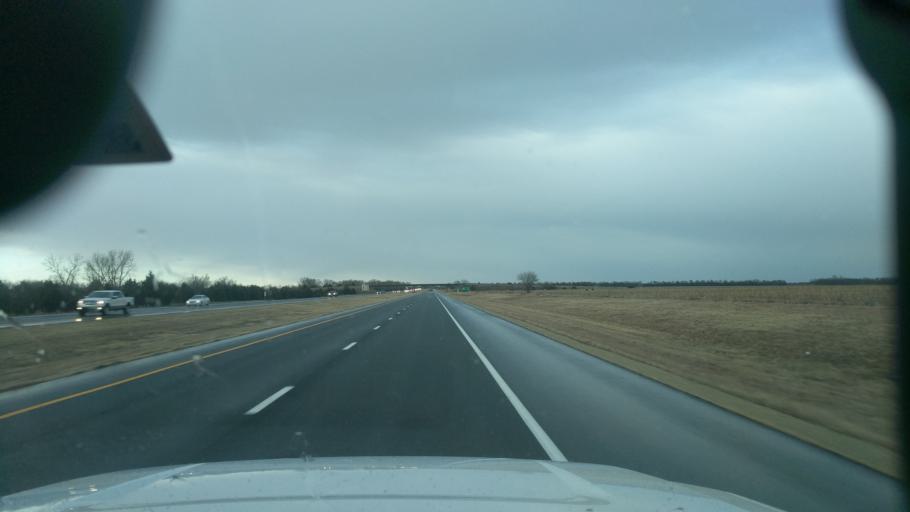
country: US
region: Kansas
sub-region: Harvey County
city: Newton
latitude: 37.9650
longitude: -97.3273
